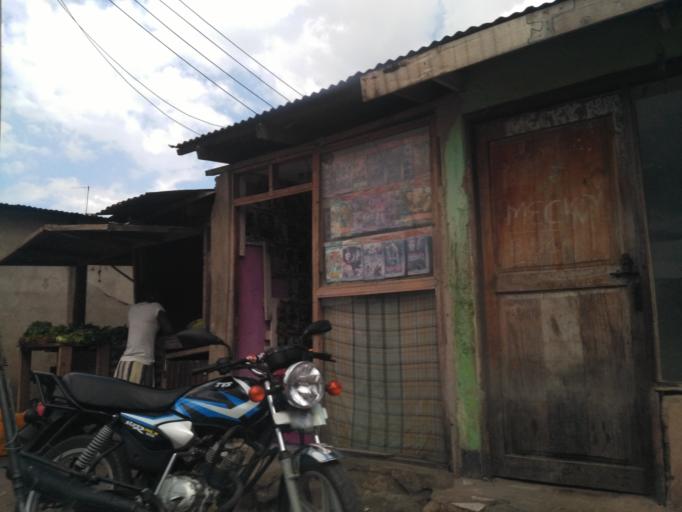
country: TZ
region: Dar es Salaam
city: Magomeni
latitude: -6.8030
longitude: 39.2656
